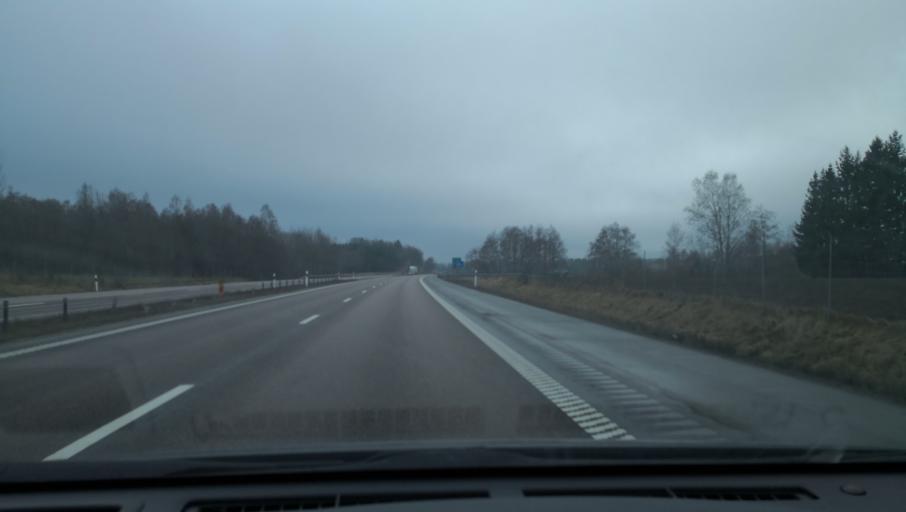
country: SE
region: OErebro
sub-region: Askersunds Kommun
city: Asbro
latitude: 59.0507
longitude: 14.9540
